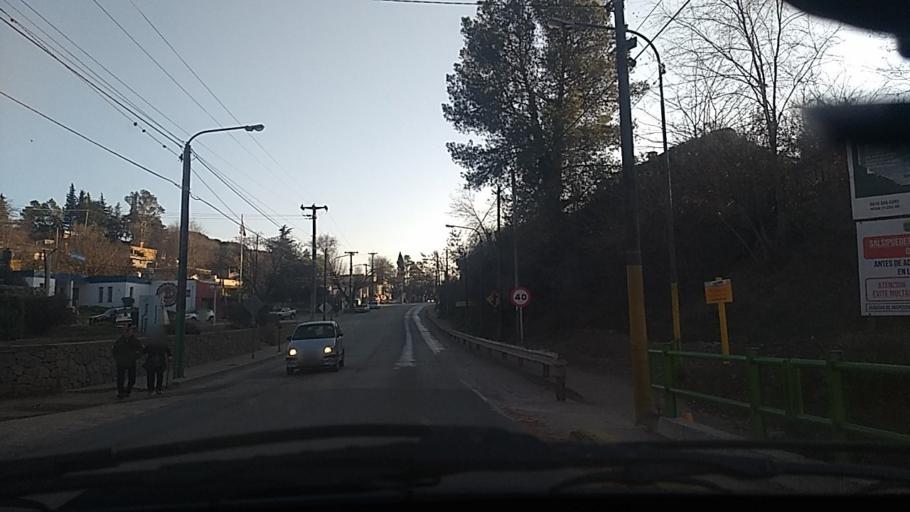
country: AR
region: Cordoba
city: Salsipuedes
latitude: -31.1388
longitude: -64.2968
